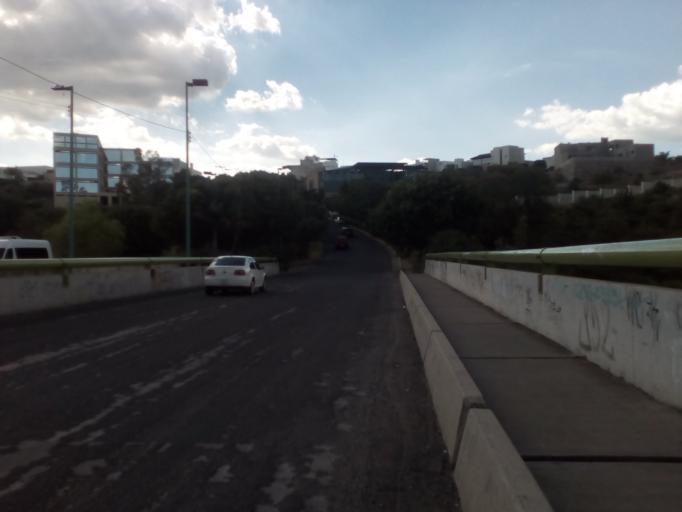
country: MX
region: Guanajuato
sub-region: Leon
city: La Ermita
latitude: 21.1524
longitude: -101.7225
